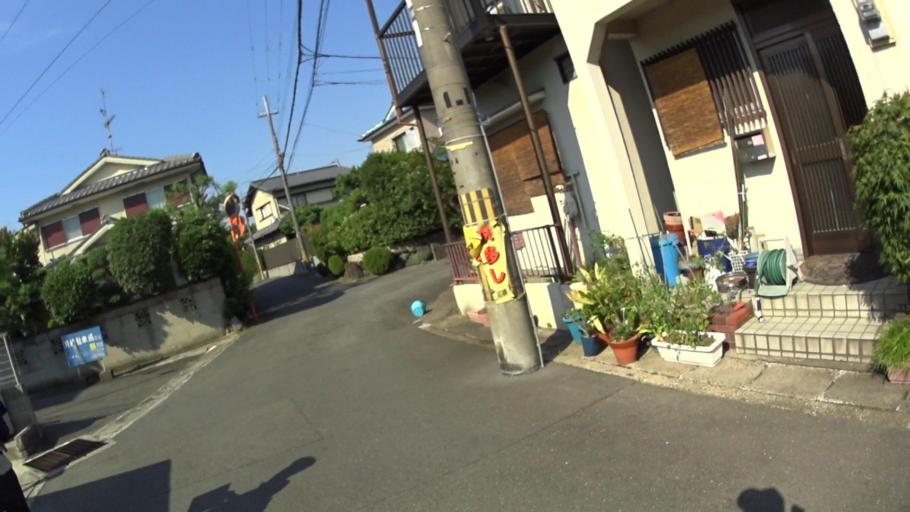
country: JP
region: Kyoto
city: Yawata
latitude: 34.9029
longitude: 135.7175
